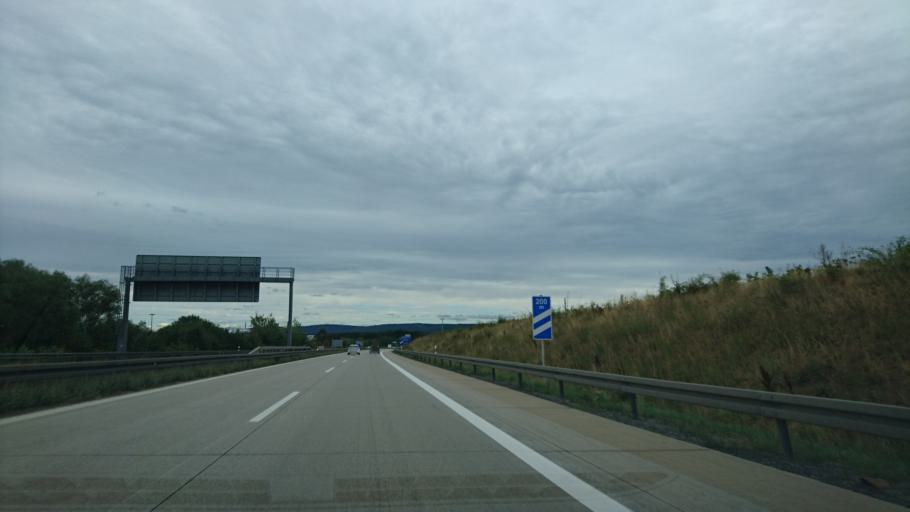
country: DE
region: Bavaria
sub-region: Upper Palatinate
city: Wernberg-Koblitz
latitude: 49.5288
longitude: 12.1468
